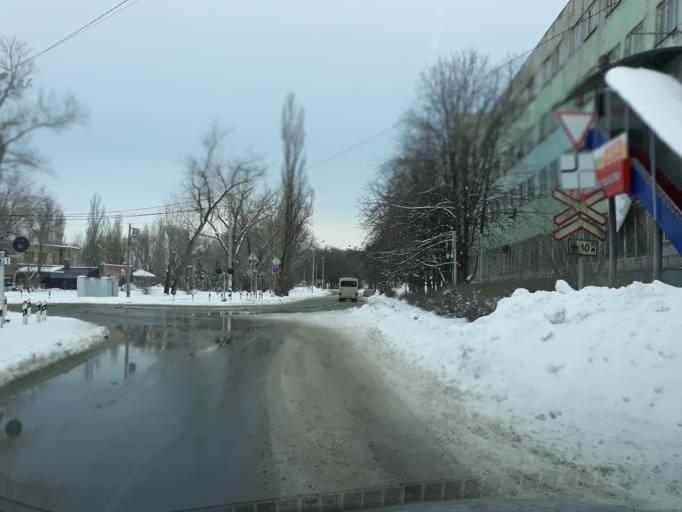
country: RU
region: Rostov
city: Taganrog
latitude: 47.2148
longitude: 38.9369
